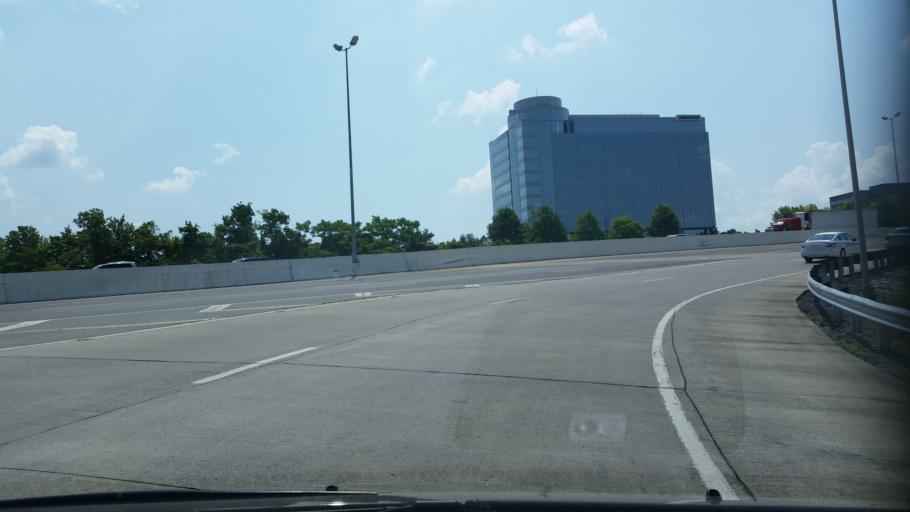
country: US
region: Tennessee
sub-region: Davidson County
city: Nashville
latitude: 36.1526
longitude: -86.6914
